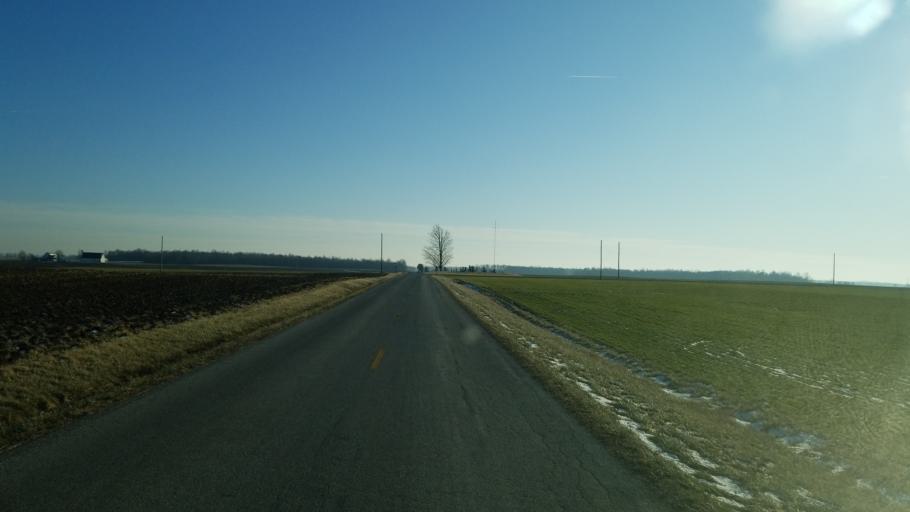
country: US
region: Ohio
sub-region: Crawford County
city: Bucyrus
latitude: 40.9962
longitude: -82.9587
